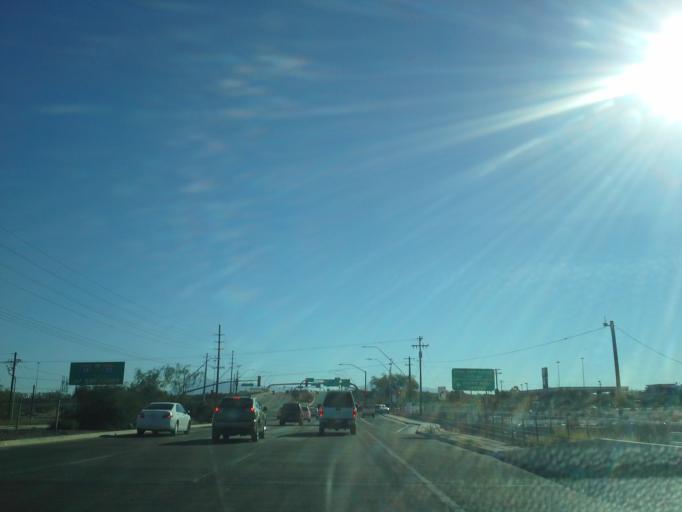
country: US
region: Arizona
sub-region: Pima County
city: Drexel Heights
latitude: 32.1337
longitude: -110.9923
